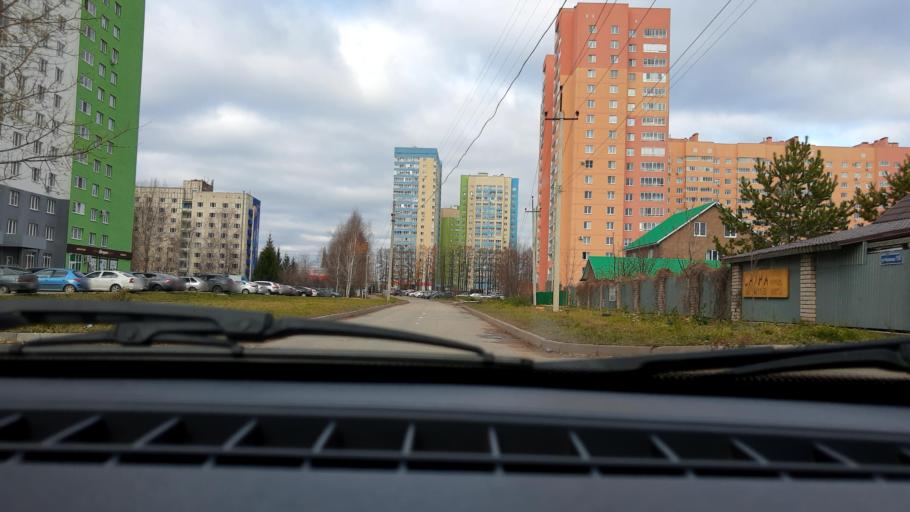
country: RU
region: Bashkortostan
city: Mikhaylovka
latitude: 54.7923
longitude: 55.8689
